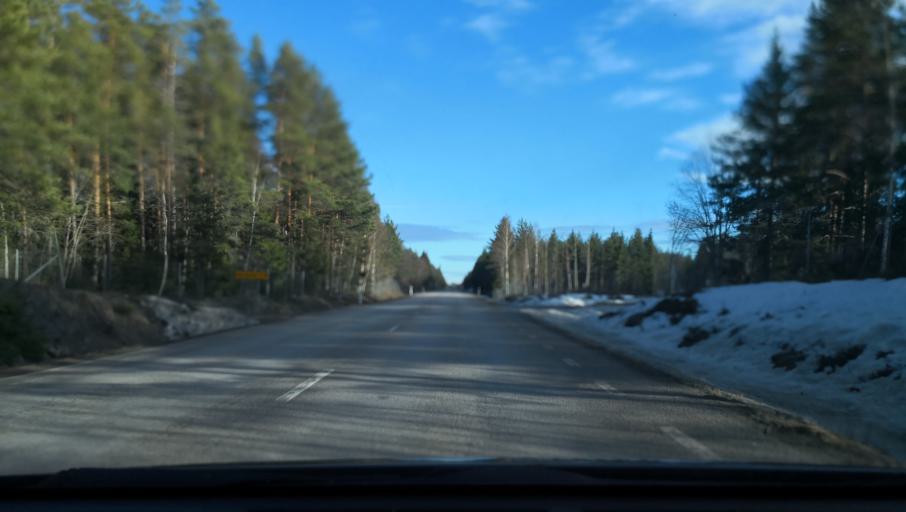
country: SE
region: Uppsala
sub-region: Osthammars Kommun
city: Osterbybruk
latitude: 60.1713
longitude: 17.9341
